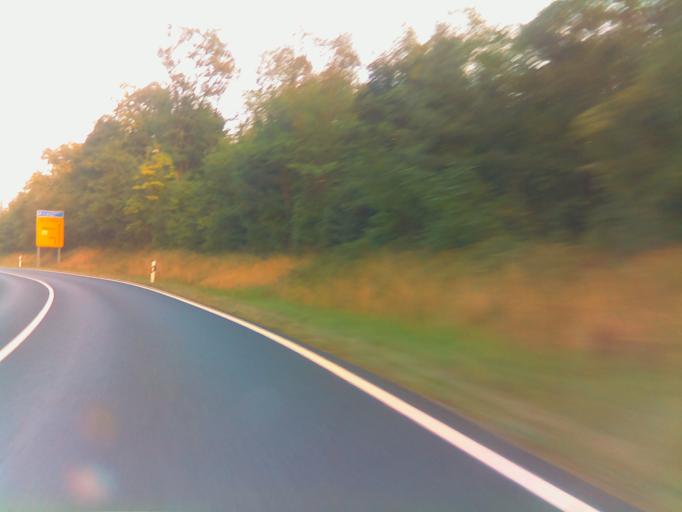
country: DE
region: Bavaria
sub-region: Regierungsbezirk Unterfranken
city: Oerlenbach
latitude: 50.1502
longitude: 10.1066
